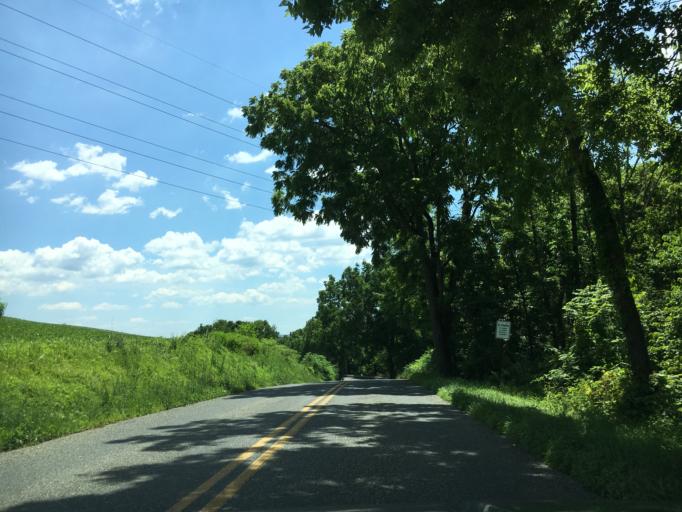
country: US
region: Pennsylvania
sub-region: Lehigh County
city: Schnecksville
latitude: 40.6694
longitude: -75.5783
